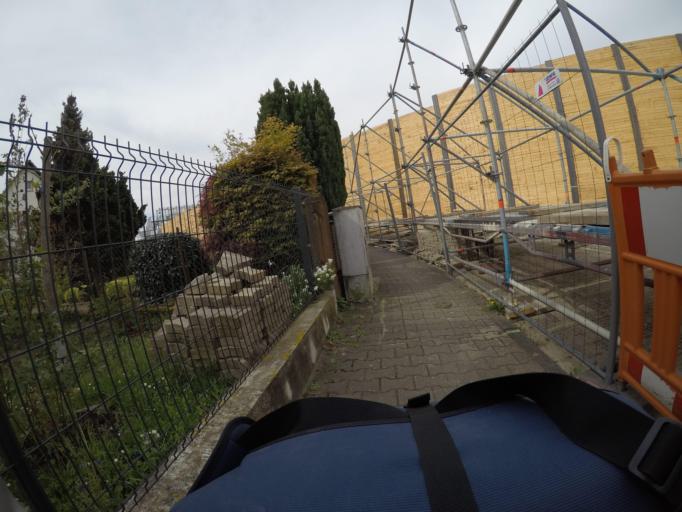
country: DE
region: Baden-Wuerttemberg
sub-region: Karlsruhe Region
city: Rastatt
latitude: 48.8447
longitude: 8.2150
